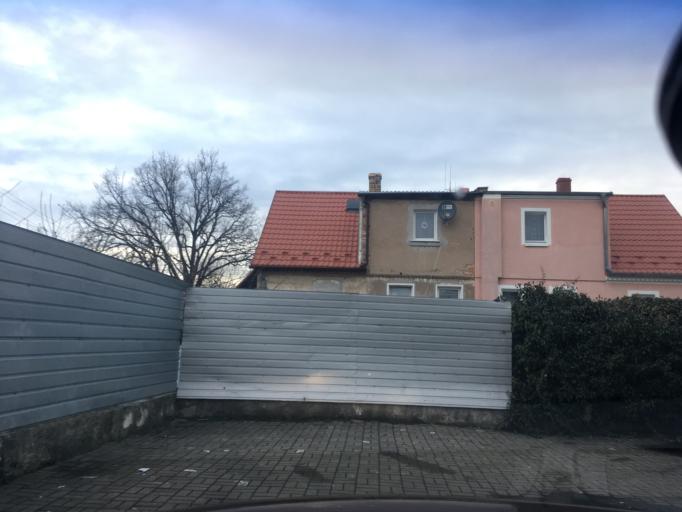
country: PL
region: Lower Silesian Voivodeship
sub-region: Powiat zgorzelecki
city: Bogatynia
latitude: 50.9020
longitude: 14.9608
